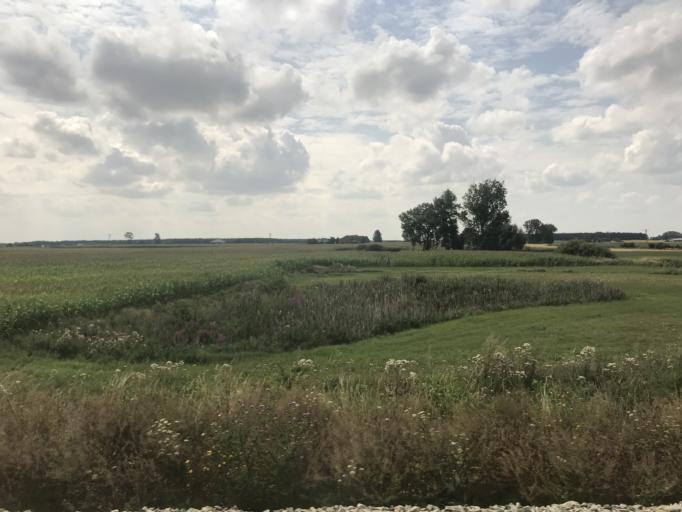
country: PL
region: Greater Poland Voivodeship
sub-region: Powiat gnieznienski
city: Lubowo
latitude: 52.5042
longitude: 17.4707
